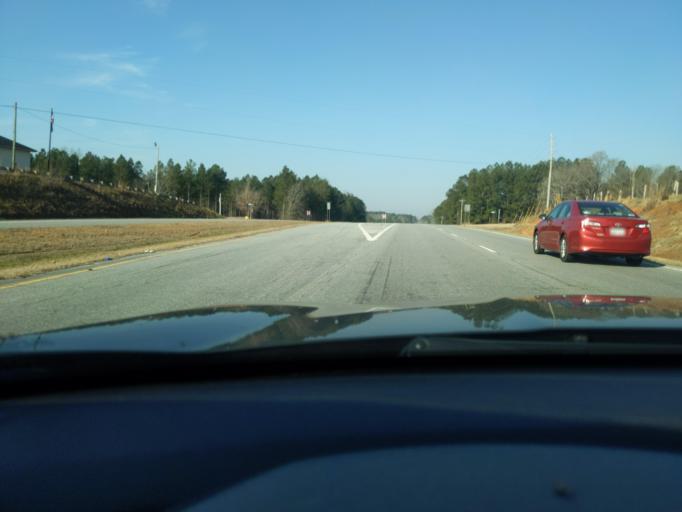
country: US
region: South Carolina
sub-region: Abbeville County
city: Abbeville
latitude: 34.1842
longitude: -82.3193
